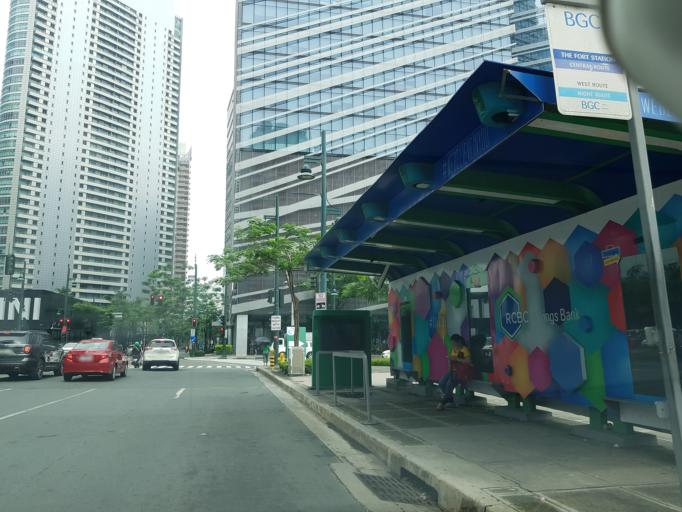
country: PH
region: Metro Manila
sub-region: Makati City
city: Makati City
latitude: 14.5489
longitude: 121.0475
